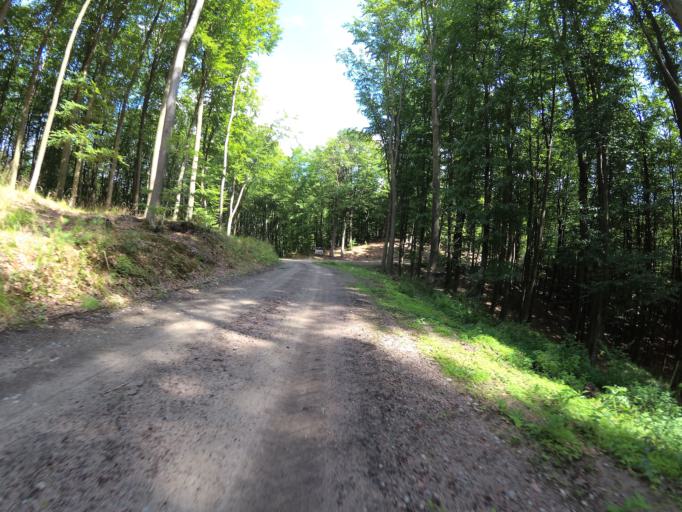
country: PL
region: Pomeranian Voivodeship
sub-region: Powiat wejherowski
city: Bojano
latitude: 54.5175
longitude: 18.4255
